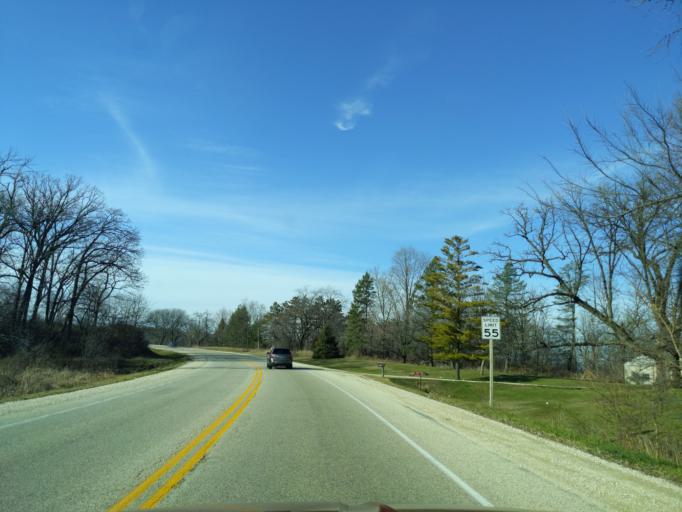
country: US
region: Wisconsin
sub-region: Rock County
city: Milton
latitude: 42.8229
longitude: -88.9327
